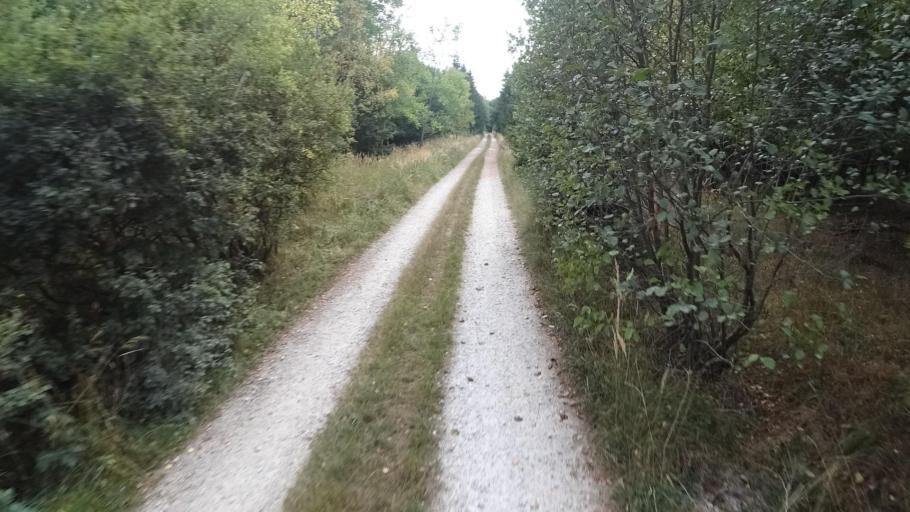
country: DE
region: Rheinland-Pfalz
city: Dichtelbach
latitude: 50.0138
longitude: 7.7141
